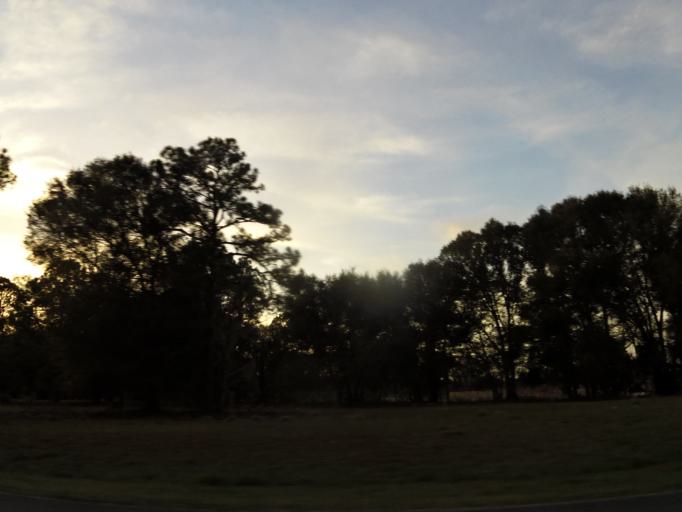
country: US
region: Florida
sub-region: Volusia County
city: De Leon Springs
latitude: 29.1122
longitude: -81.2917
